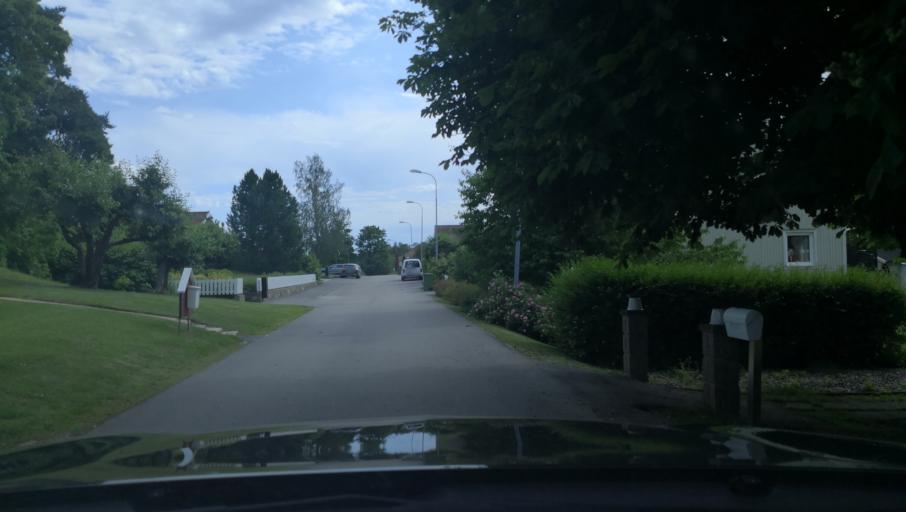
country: SE
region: Vaestmanland
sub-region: Fagersta Kommun
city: Fagersta
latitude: 59.9873
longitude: 15.8278
